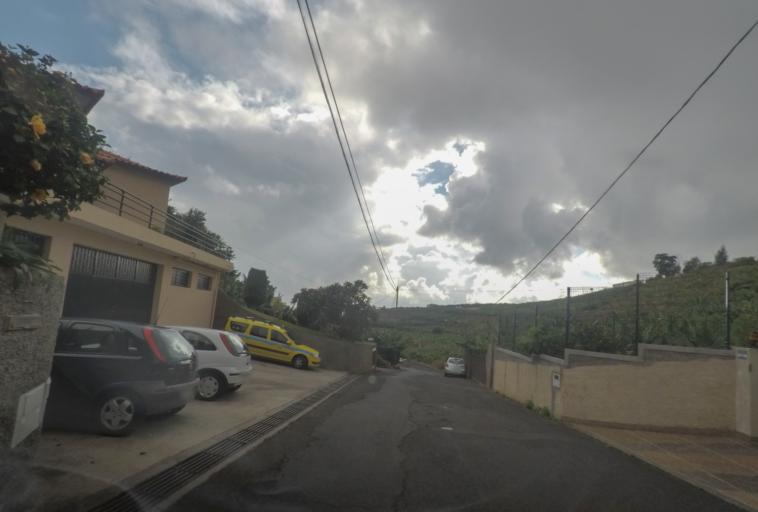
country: PT
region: Madeira
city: Camara de Lobos
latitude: 32.6571
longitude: -16.9582
